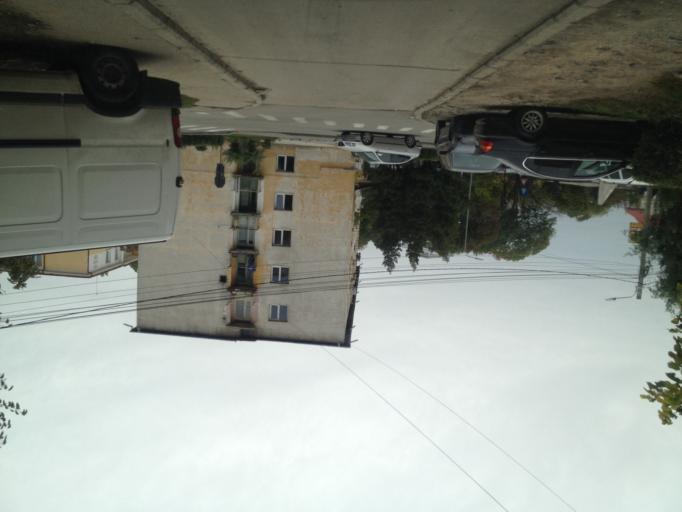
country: RO
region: Dolj
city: Craiova
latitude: 44.3284
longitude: 23.7805
